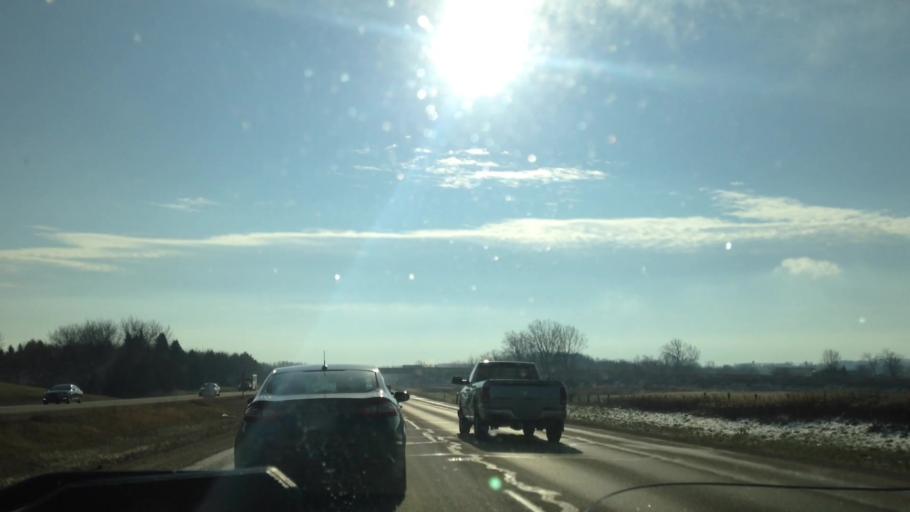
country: US
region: Wisconsin
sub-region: Washington County
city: Slinger
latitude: 43.3133
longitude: -88.2355
